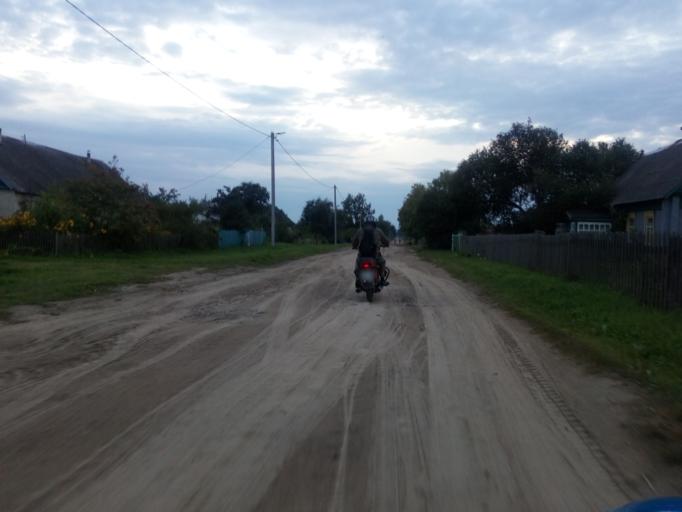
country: BY
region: Vitebsk
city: Dzisna
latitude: 55.6707
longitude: 28.3156
